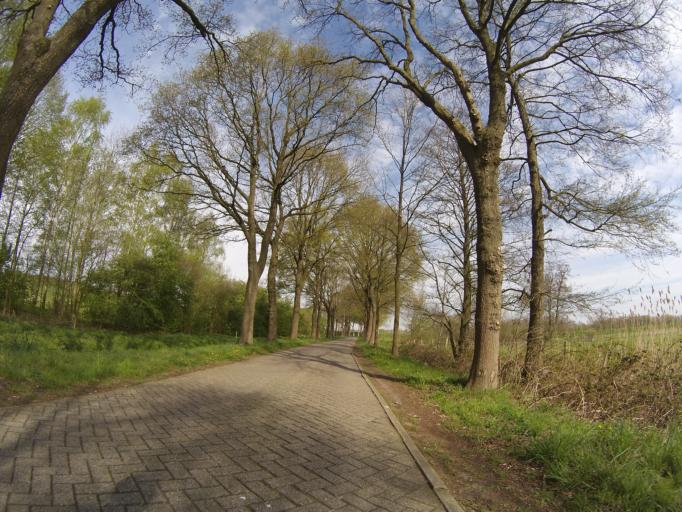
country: NL
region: Drenthe
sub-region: Gemeente Coevorden
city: Sleen
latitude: 52.8031
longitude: 6.7076
